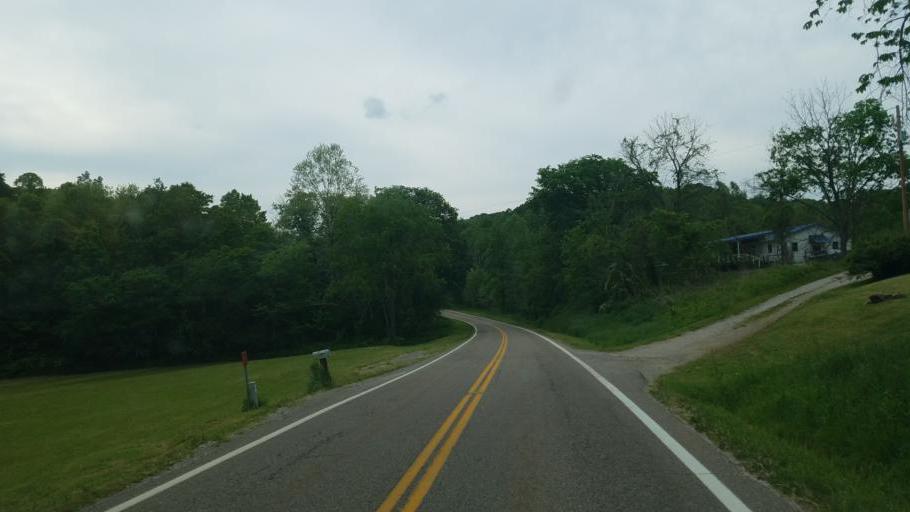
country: US
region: Ohio
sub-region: Meigs County
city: Pomeroy
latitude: 39.1363
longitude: -82.1483
